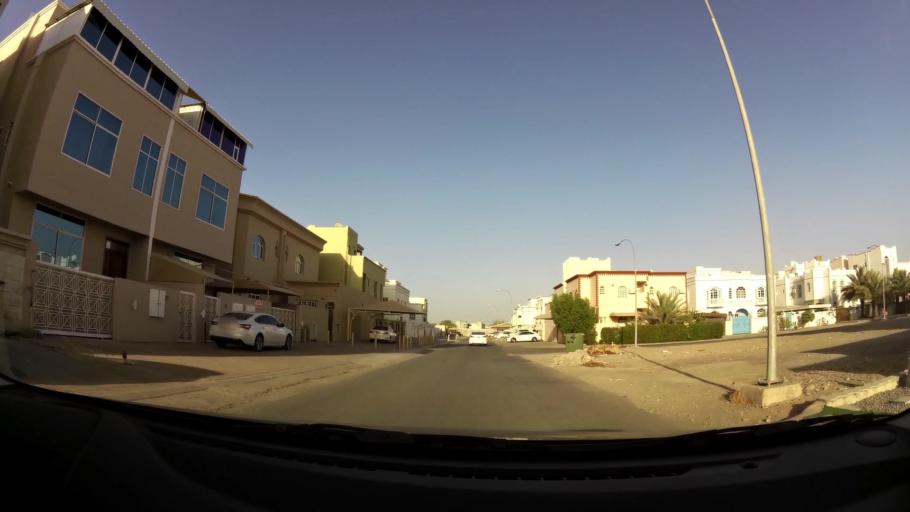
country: OM
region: Muhafazat Masqat
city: As Sib al Jadidah
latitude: 23.6125
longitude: 58.2300
